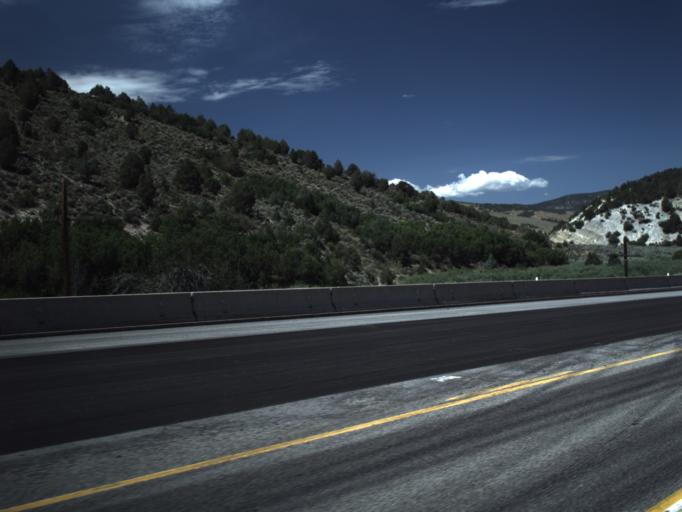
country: US
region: Utah
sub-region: Utah County
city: Mapleton
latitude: 39.9537
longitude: -111.2630
